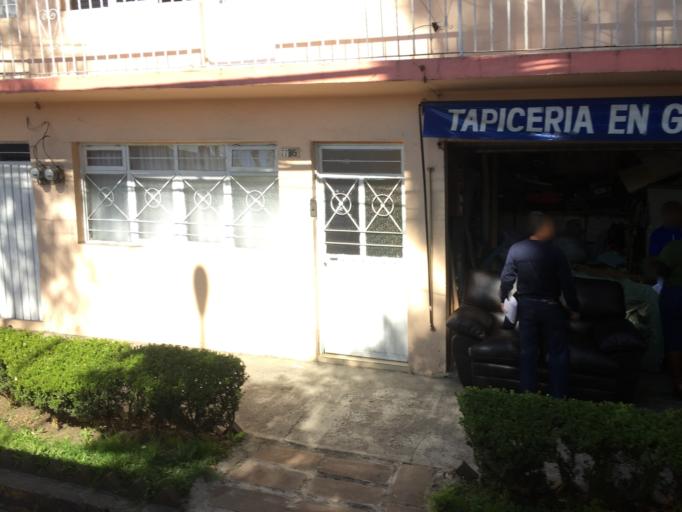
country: MX
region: Veracruz
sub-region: Xalapa
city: Xalapa de Enriquez
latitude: 19.5419
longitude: -96.9237
